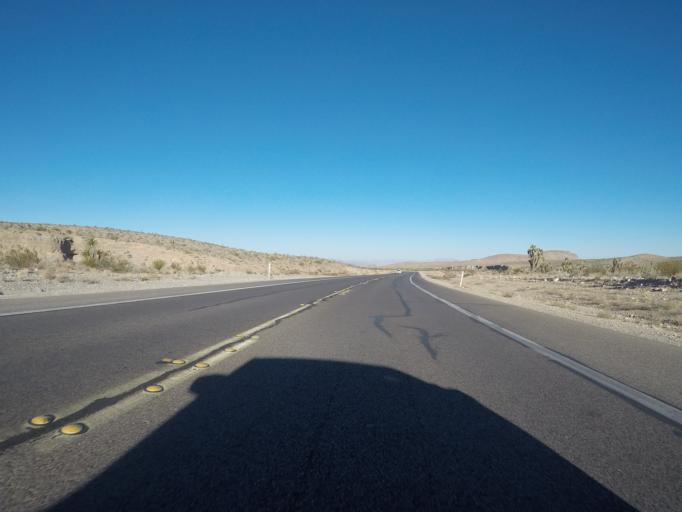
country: US
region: Nevada
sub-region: Clark County
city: Summerlin South
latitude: 36.1328
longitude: -115.4156
